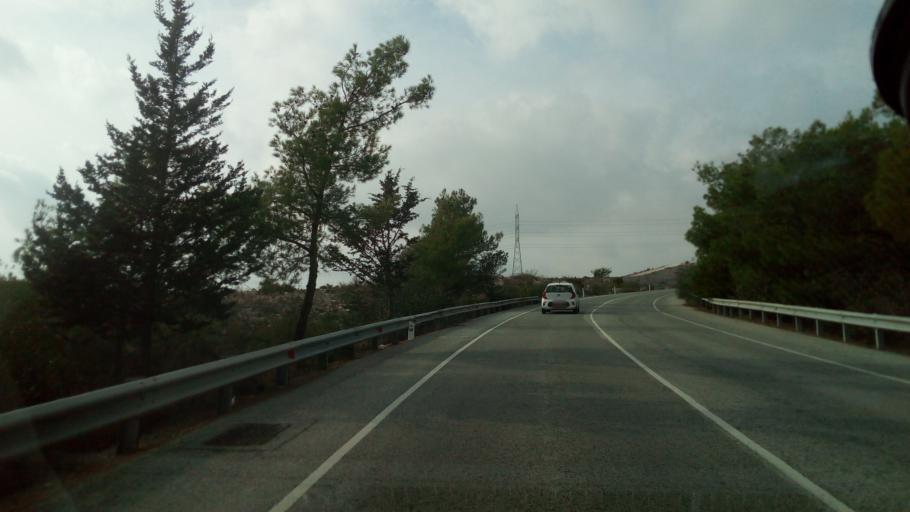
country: CY
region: Larnaka
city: Kofinou
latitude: 34.8404
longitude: 33.3333
